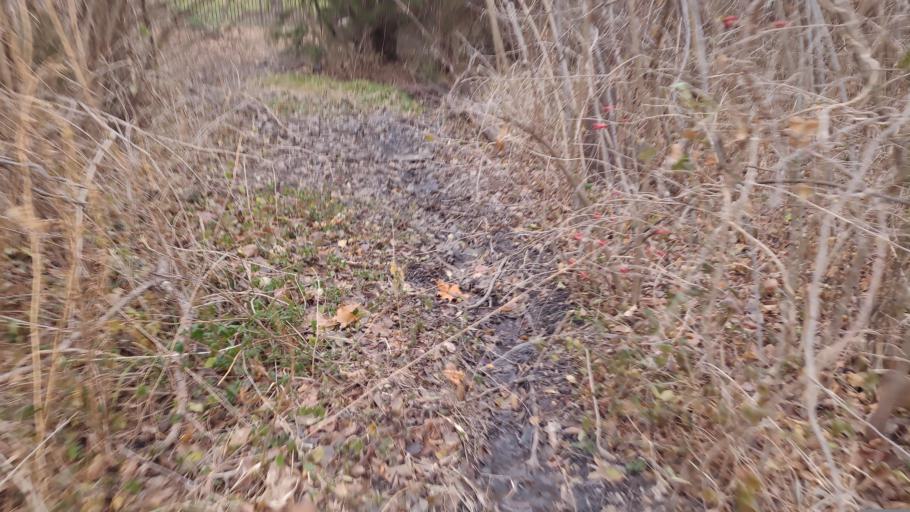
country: US
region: Kansas
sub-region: Douglas County
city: Lawrence
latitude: 38.9814
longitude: -95.2802
